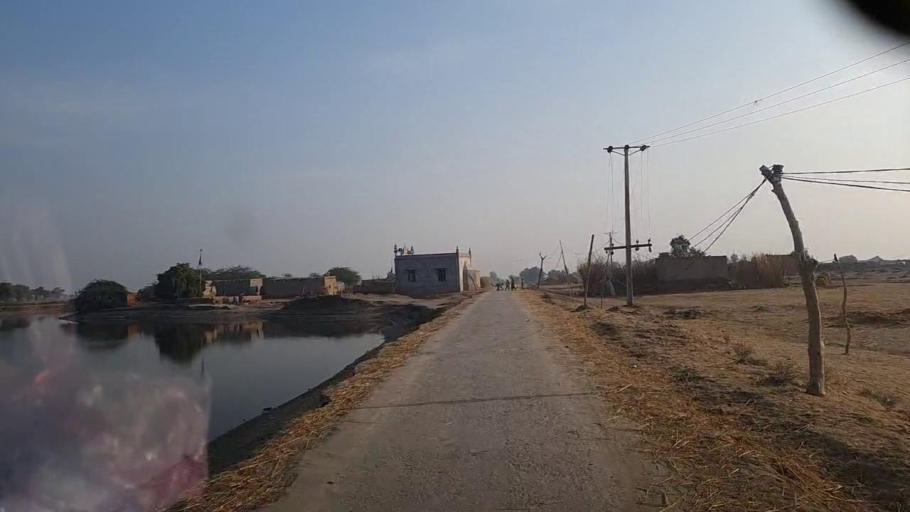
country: PK
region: Sindh
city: Jacobabad
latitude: 28.2367
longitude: 68.4842
